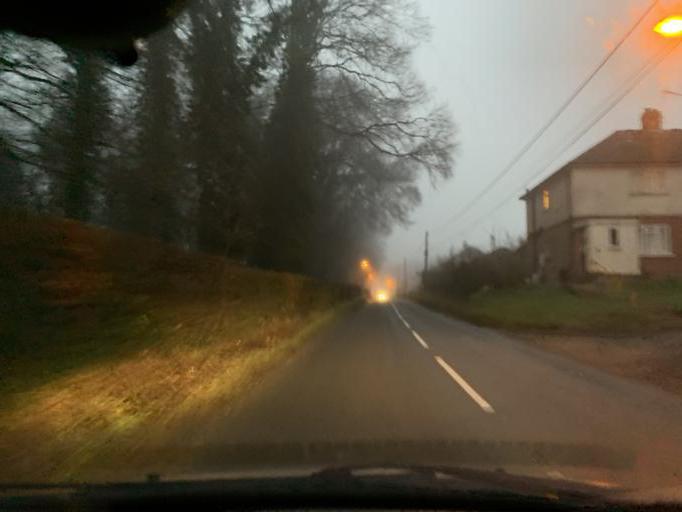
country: GB
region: England
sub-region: Wiltshire
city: Shrewton
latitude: 51.2006
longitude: -1.8929
